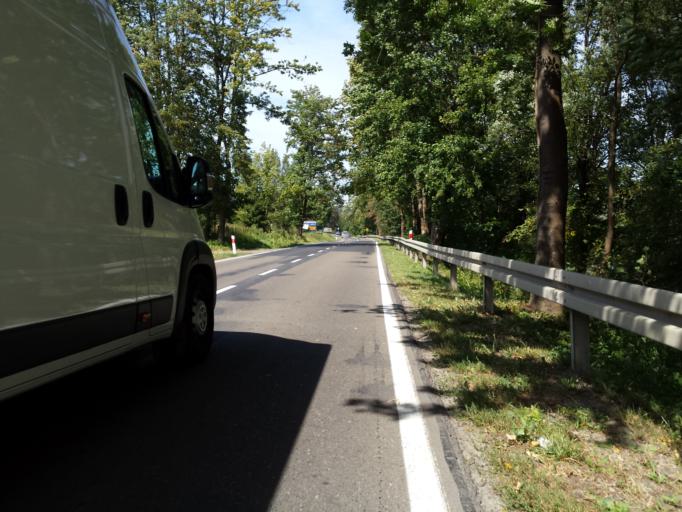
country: PL
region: Subcarpathian Voivodeship
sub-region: Powiat leski
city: Lesko
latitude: 49.4606
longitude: 22.3332
